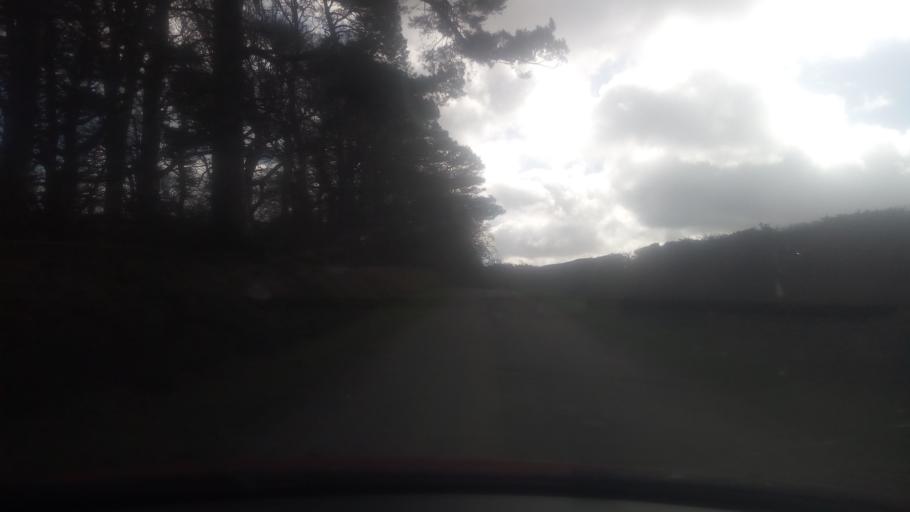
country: GB
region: Scotland
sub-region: The Scottish Borders
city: Saint Boswells
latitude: 55.5520
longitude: -2.5944
